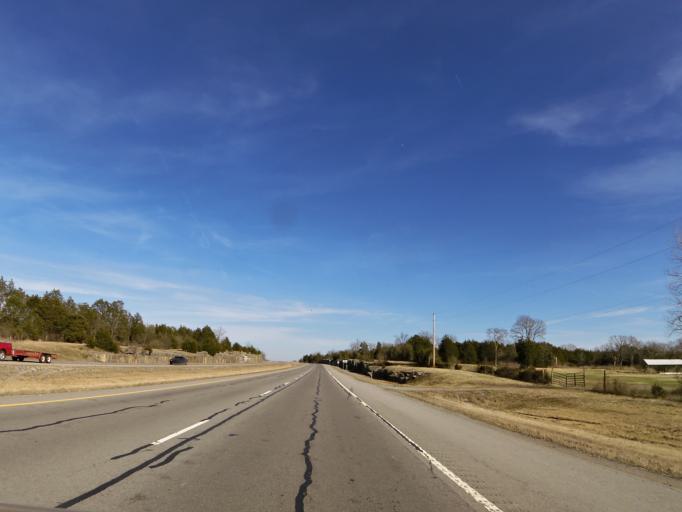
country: US
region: Tennessee
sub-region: Rutherford County
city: Murfreesboro
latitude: 35.8307
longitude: -86.3303
